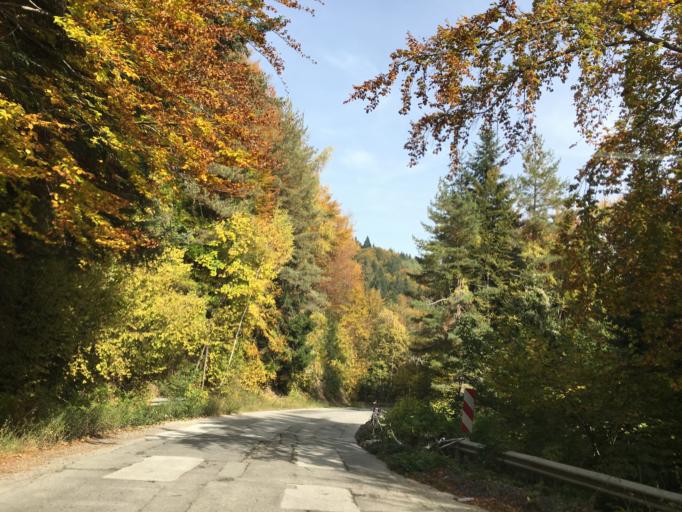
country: BG
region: Sofiya
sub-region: Obshtina Samokov
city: Samokov
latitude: 42.2839
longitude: 23.6433
